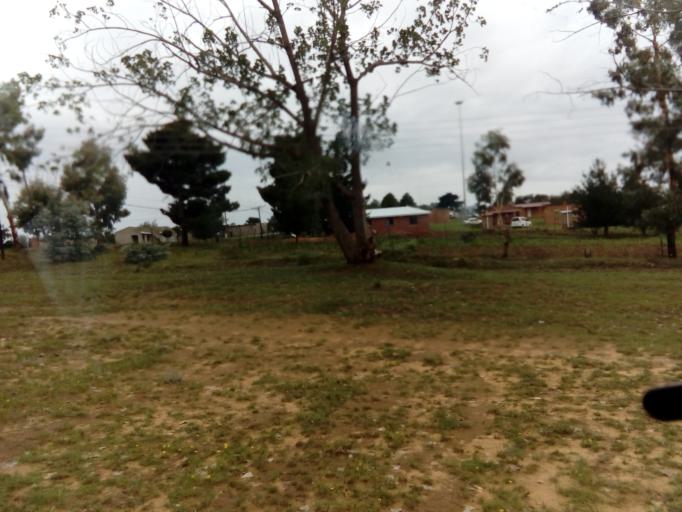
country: LS
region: Berea
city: Teyateyaneng
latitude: -29.1069
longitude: 27.9628
